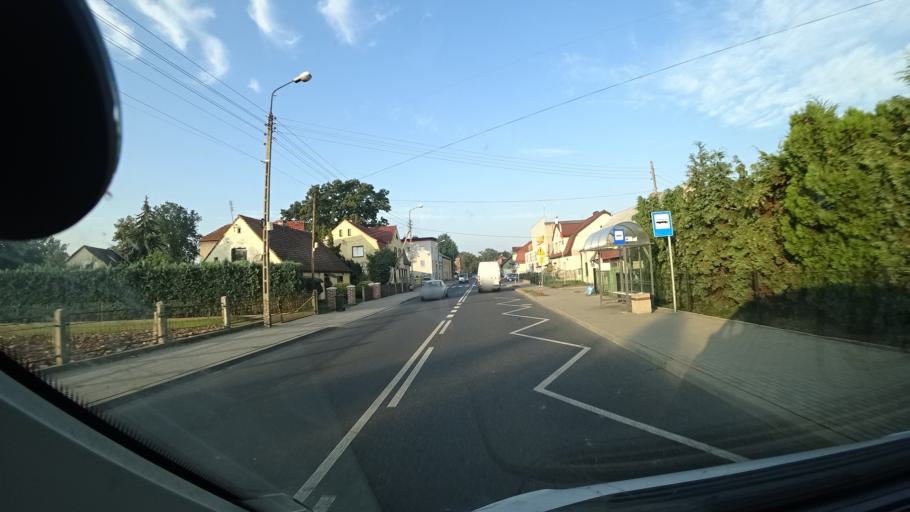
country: PL
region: Opole Voivodeship
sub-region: Powiat kedzierzynsko-kozielski
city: Slawiecice
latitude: 50.3727
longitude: 18.3236
